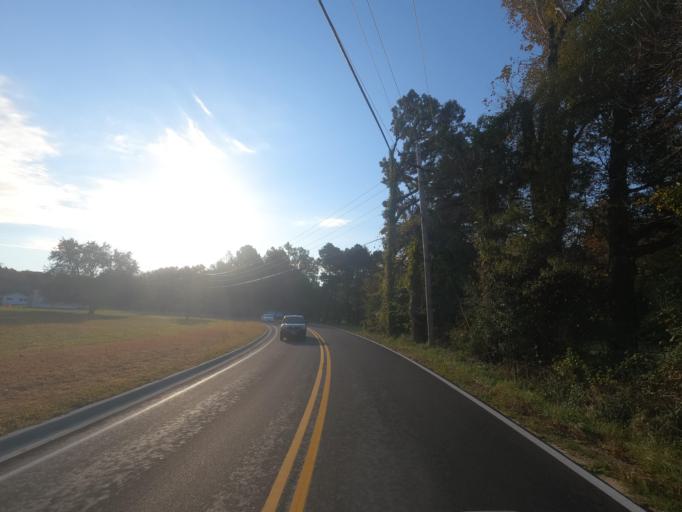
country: US
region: Maryland
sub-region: Saint Mary's County
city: Golden Beach
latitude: 38.4970
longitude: -76.6354
